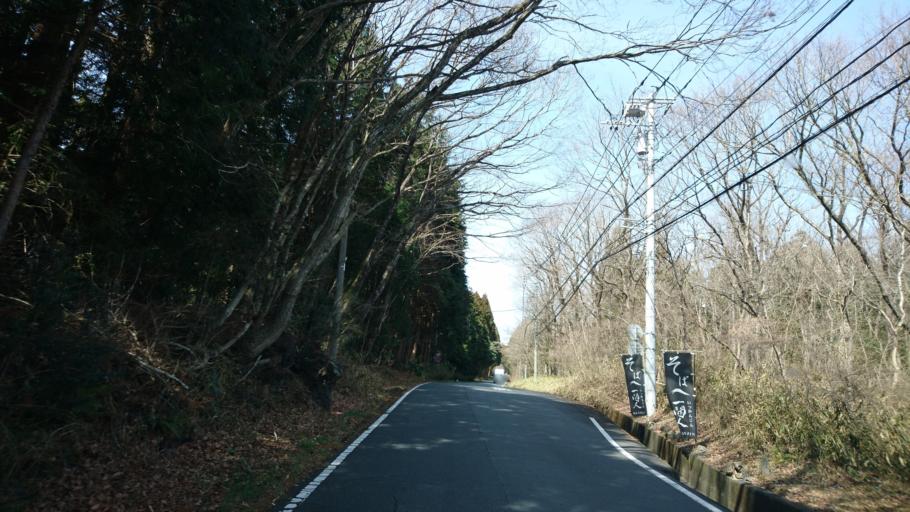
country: JP
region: Shizuoka
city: Fujinomiya
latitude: 35.3391
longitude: 138.5741
